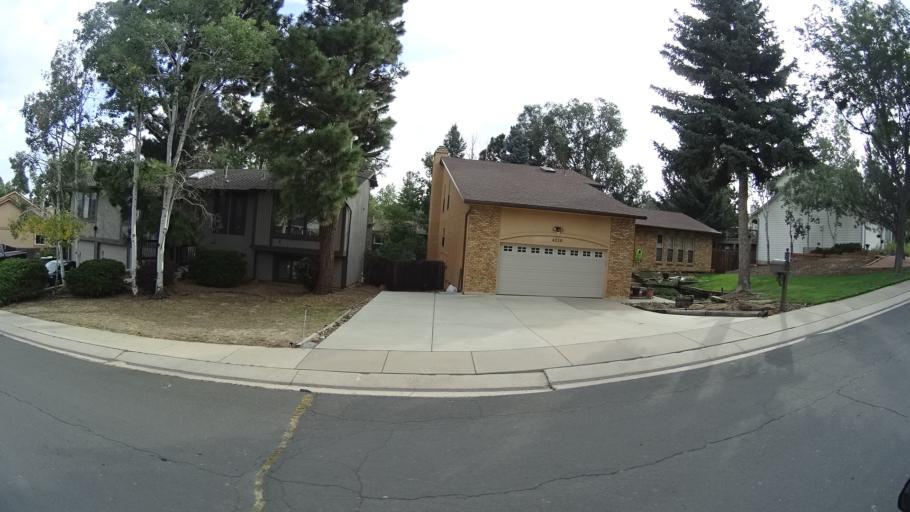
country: US
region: Colorado
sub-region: El Paso County
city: Cimarron Hills
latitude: 38.8697
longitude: -104.7497
